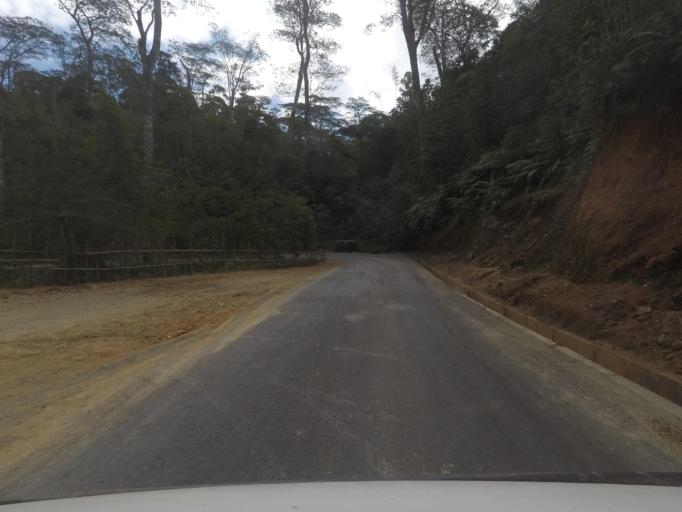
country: TL
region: Ermera
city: Gleno
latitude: -8.7462
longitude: 125.3467
